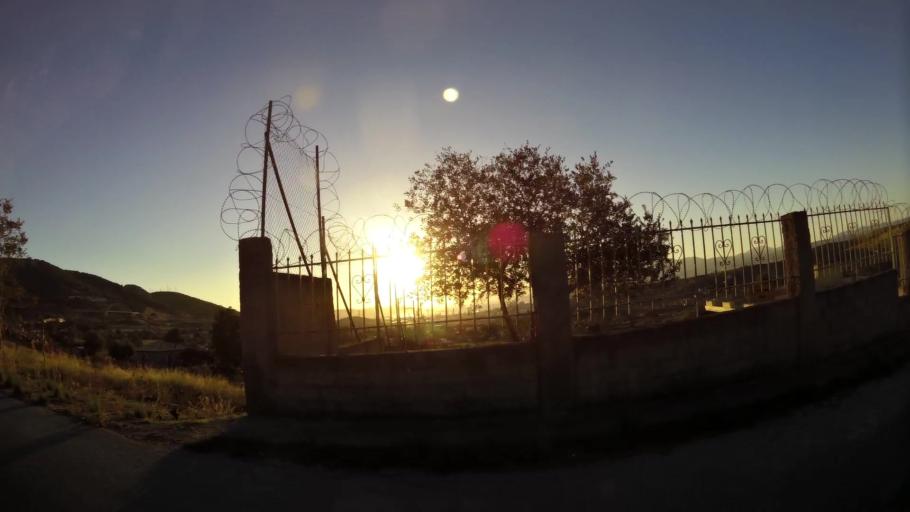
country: GR
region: Attica
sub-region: Nomarchia Athinas
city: Chaidari
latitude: 38.0390
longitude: 23.6372
